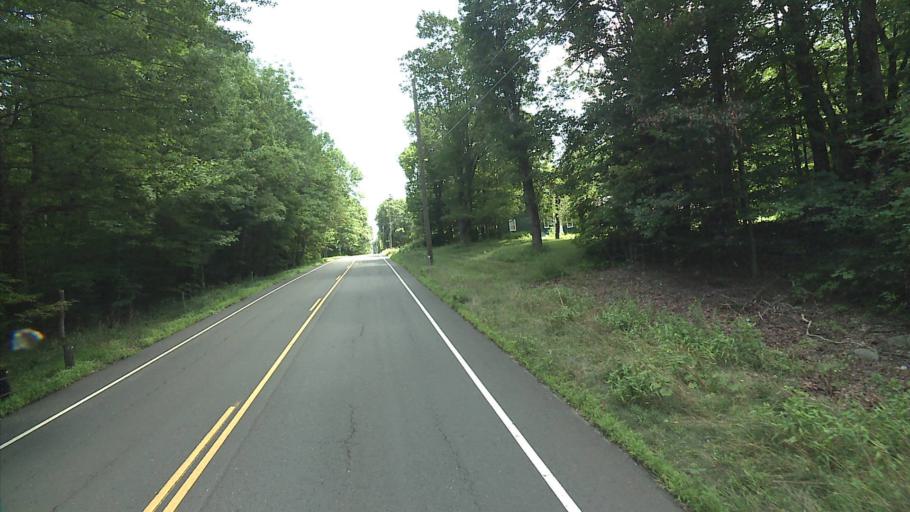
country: US
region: Massachusetts
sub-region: Hampden County
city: Granville
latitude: 42.0112
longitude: -72.9138
